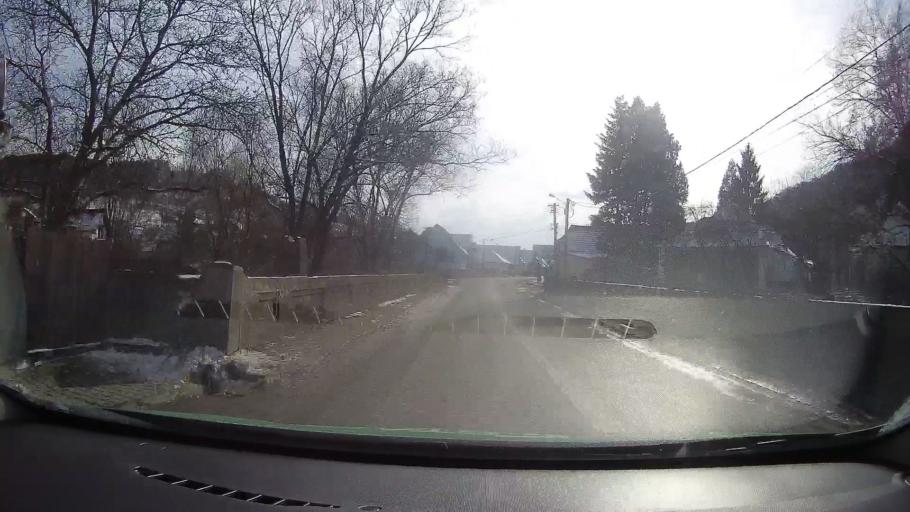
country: RO
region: Mures
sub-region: Municipiul Sighisoara
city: Sighisoara
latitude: 46.2143
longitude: 24.7824
